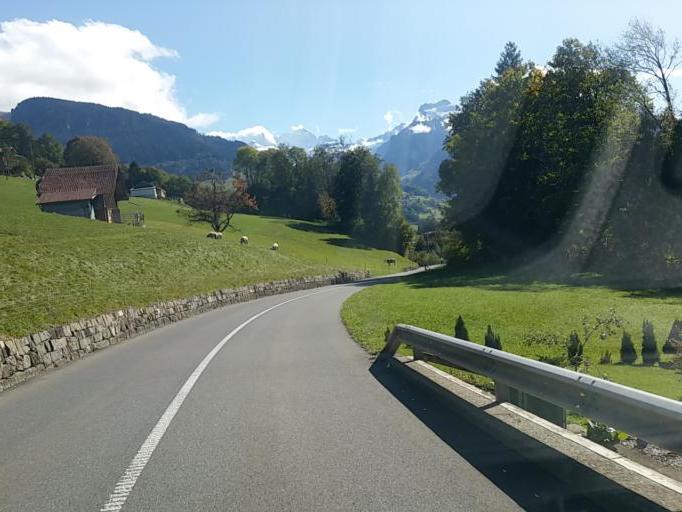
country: CH
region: Bern
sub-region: Frutigen-Niedersimmental District
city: Aeschi
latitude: 46.6488
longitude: 7.6892
